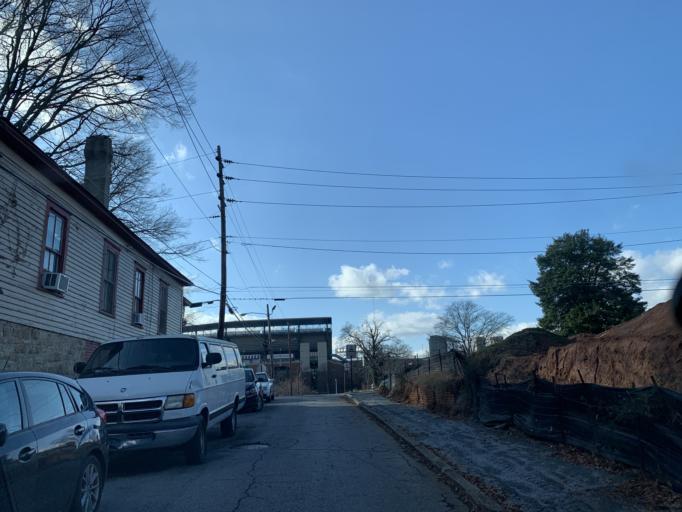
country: US
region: Georgia
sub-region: Fulton County
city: Atlanta
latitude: 33.7355
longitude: -84.3859
